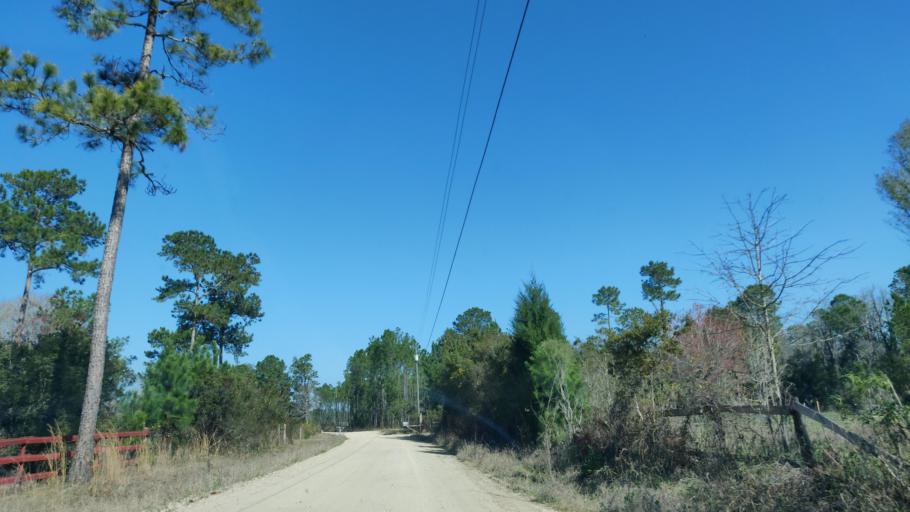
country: US
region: Florida
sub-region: Duval County
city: Baldwin
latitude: 30.1737
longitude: -81.9570
